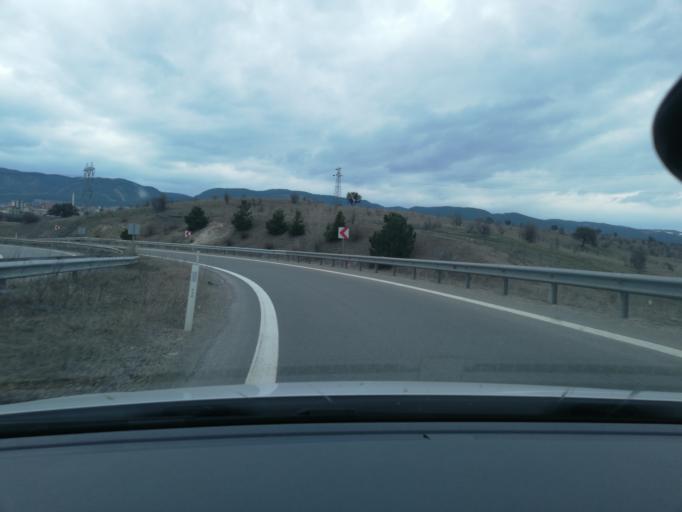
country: TR
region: Bolu
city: Gerede
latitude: 40.7778
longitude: 32.2197
